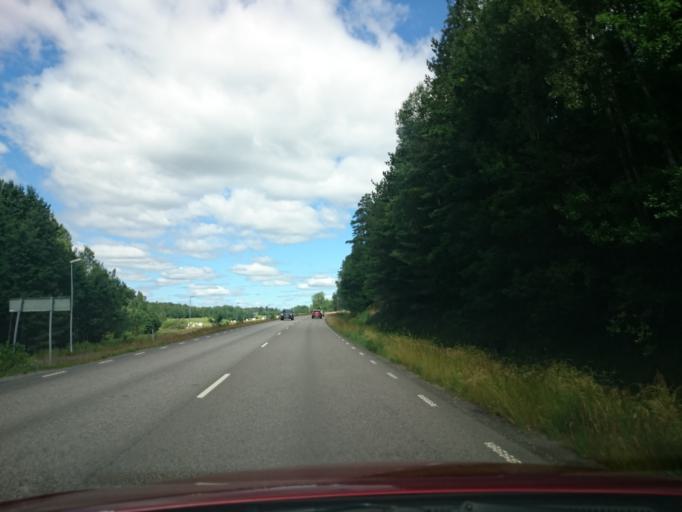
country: SE
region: Vaestra Goetaland
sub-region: Lerums Kommun
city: Stenkullen
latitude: 57.8068
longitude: 12.3038
